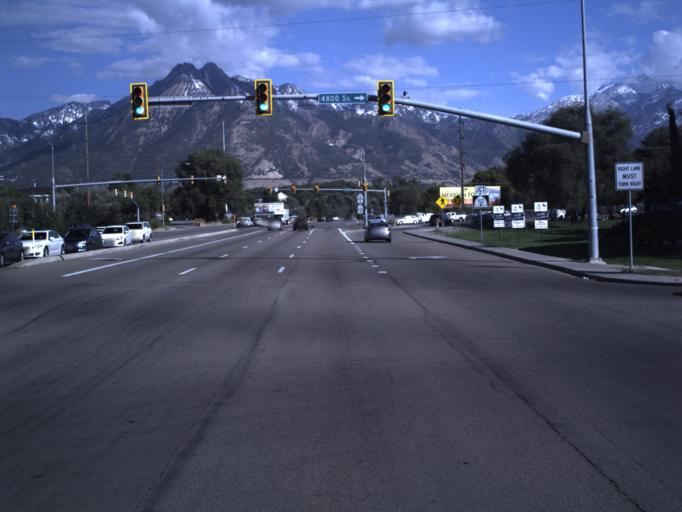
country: US
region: Utah
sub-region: Salt Lake County
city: Murray
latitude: 40.6659
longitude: -111.8666
